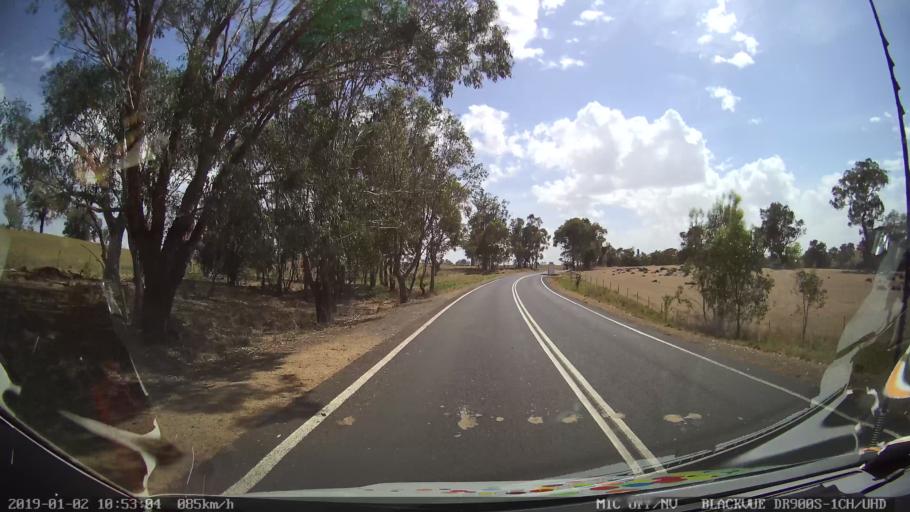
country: AU
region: New South Wales
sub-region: Cootamundra
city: Cootamundra
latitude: -34.6814
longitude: 148.2720
